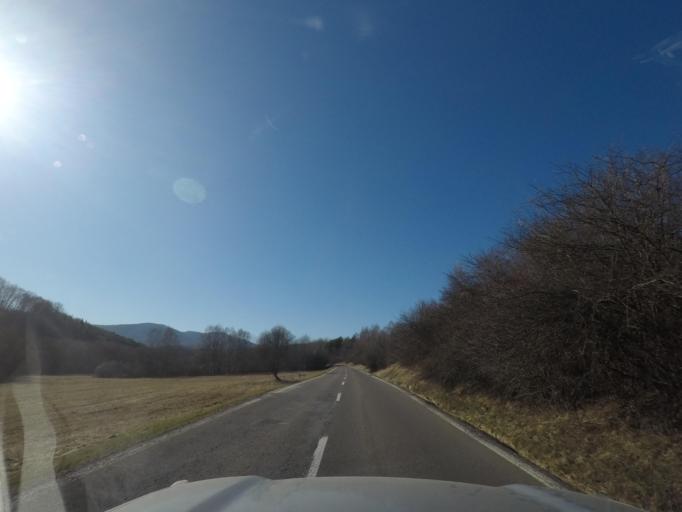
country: UA
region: Zakarpattia
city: Velykyi Bereznyi
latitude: 48.9259
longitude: 22.3392
